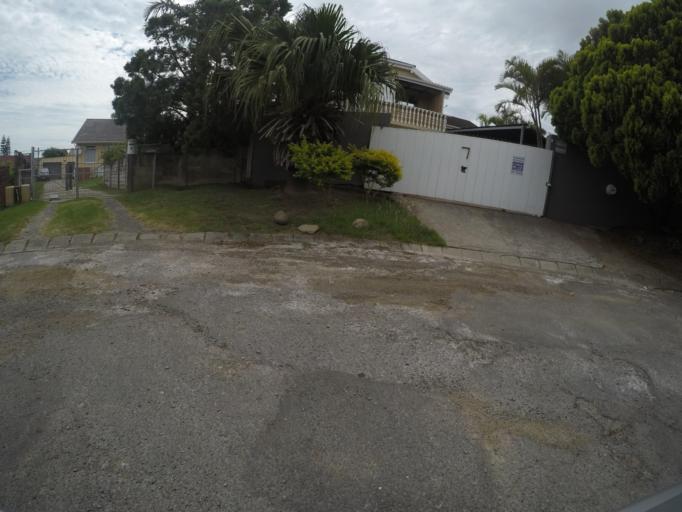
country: ZA
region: Eastern Cape
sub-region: Buffalo City Metropolitan Municipality
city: East London
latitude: -32.9928
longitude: 27.8638
